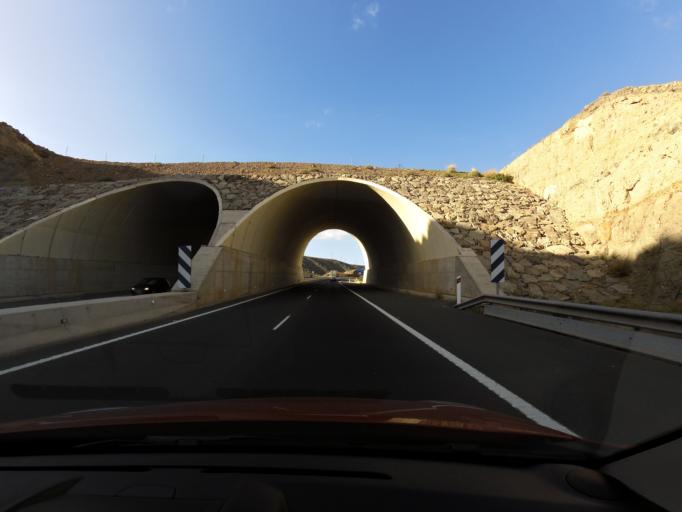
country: ES
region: Canary Islands
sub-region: Provincia de Las Palmas
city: Puerto Rico
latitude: 27.7737
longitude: -15.6750
